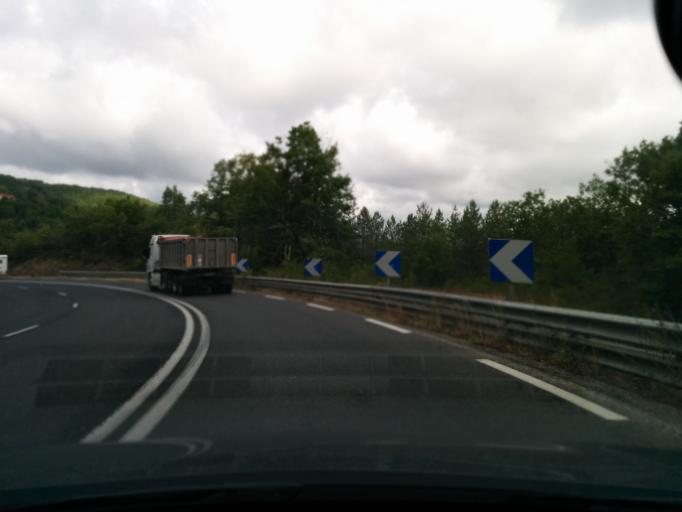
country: FR
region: Midi-Pyrenees
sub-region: Departement du Lot
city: Souillac
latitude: 44.8617
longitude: 1.4831
